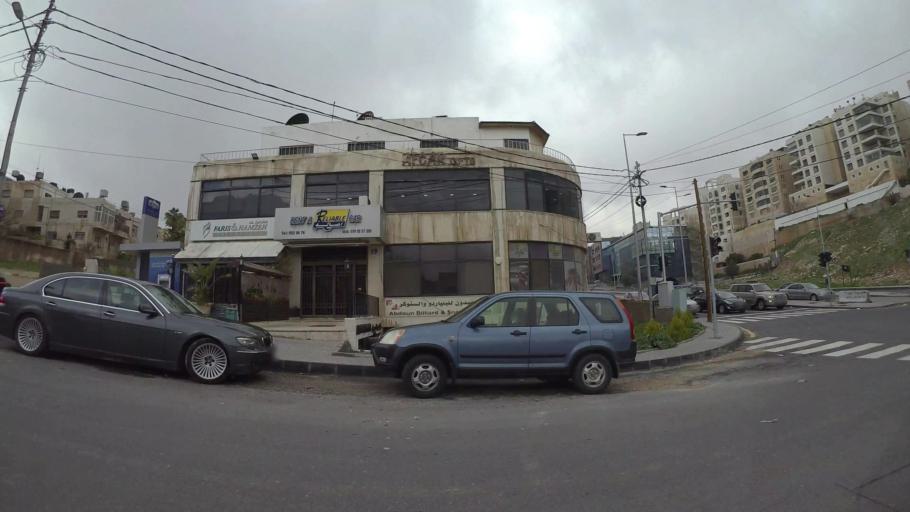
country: JO
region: Amman
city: Amman
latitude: 31.9548
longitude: 35.8845
